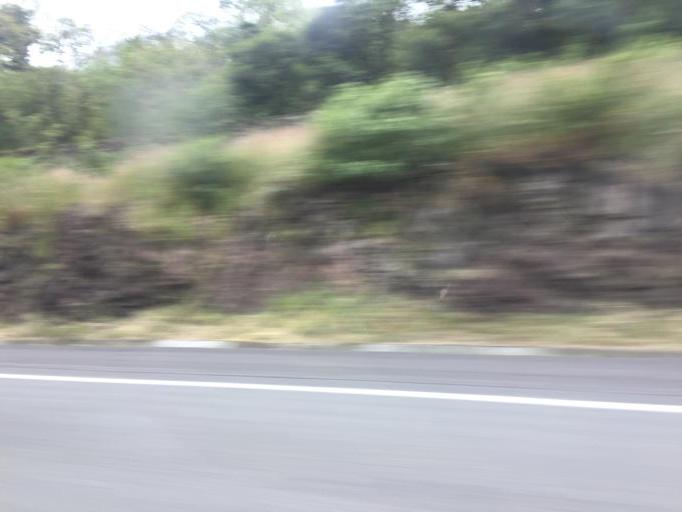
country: MX
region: Jalisco
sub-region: Zapotlan del Rey
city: Zapotlan del Rey
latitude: 20.5082
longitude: -102.9669
